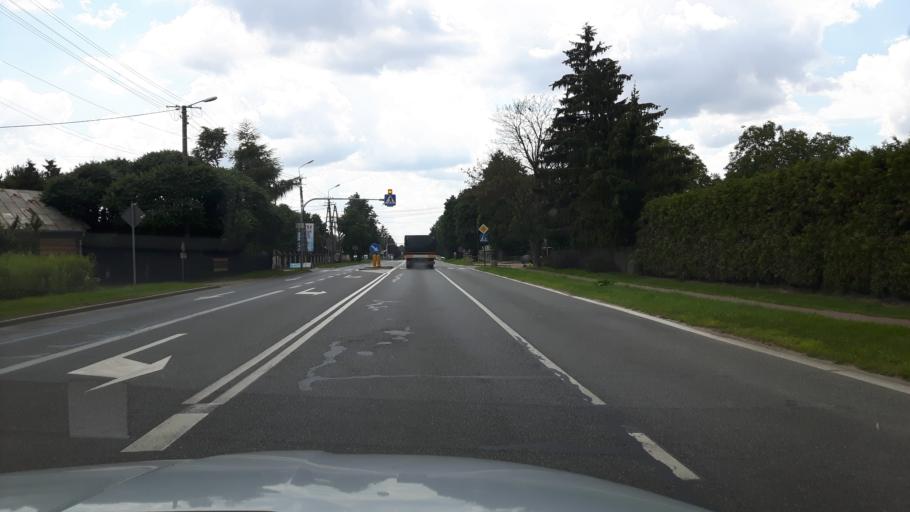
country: PL
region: Masovian Voivodeship
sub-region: Powiat wyszkowski
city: Wyszkow
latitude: 52.6011
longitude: 21.4657
